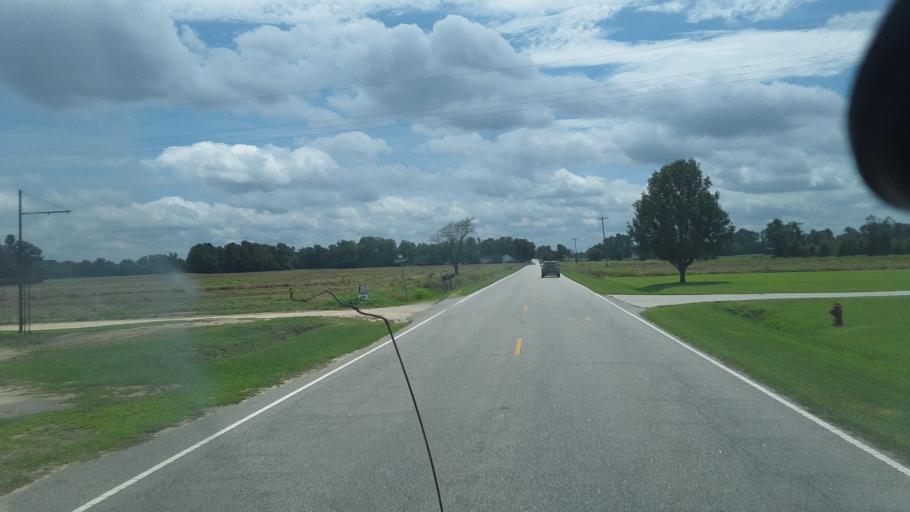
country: US
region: North Carolina
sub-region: Robeson County
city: Fairmont
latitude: 34.3896
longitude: -79.1204
